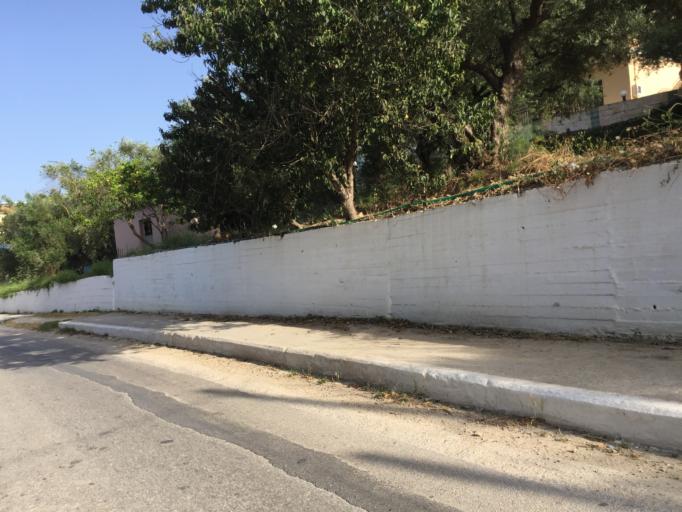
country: GR
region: Ionian Islands
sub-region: Nomos Zakynthou
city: Vanaton
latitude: 37.8197
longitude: 20.8576
